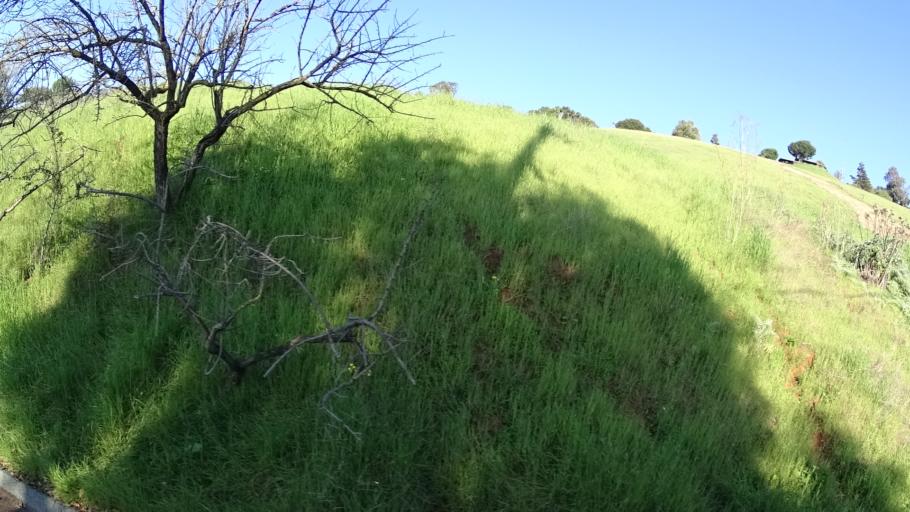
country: US
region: California
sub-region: Alameda County
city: Hayward
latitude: 37.6579
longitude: -122.0690
